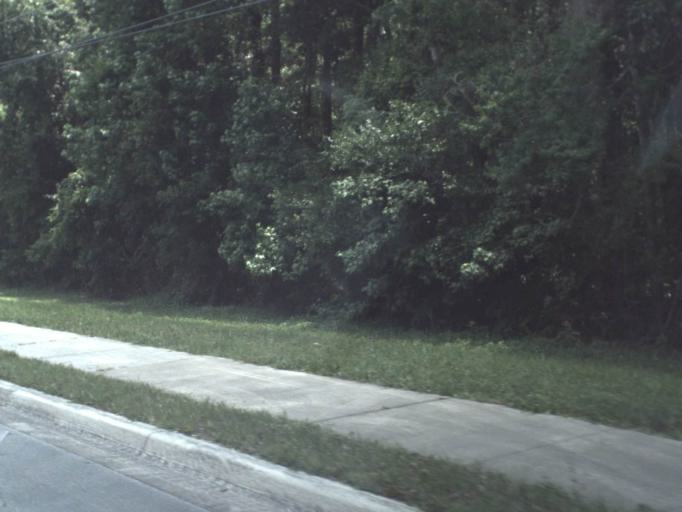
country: US
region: Florida
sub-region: Saint Johns County
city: Saint Augustine South
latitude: 29.8340
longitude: -81.3722
